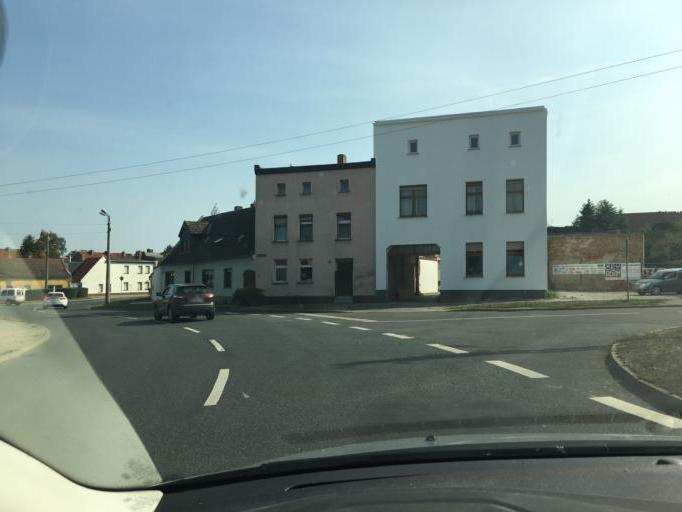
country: DE
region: Saxony-Anhalt
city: Calbe
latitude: 51.8974
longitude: 11.7712
